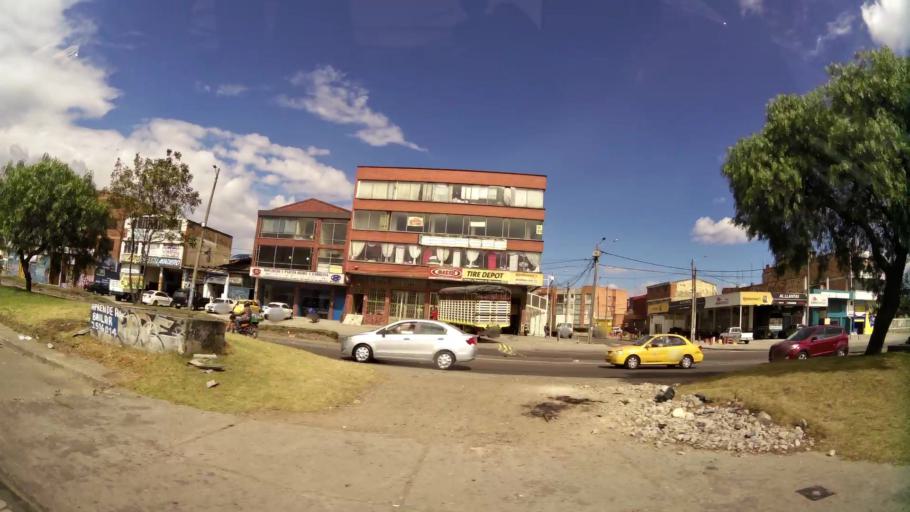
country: CO
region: Bogota D.C.
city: Bogota
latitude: 4.6142
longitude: -74.1404
